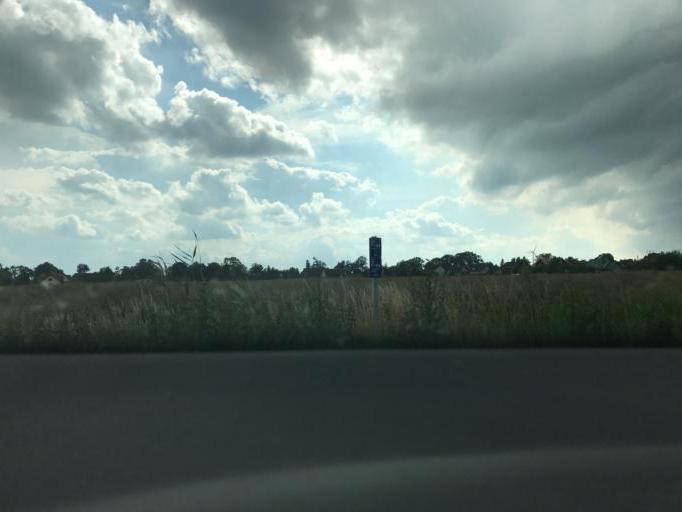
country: PL
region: Pomeranian Voivodeship
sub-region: Powiat gdanski
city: Cedry Wielkie
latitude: 54.3339
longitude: 18.8053
